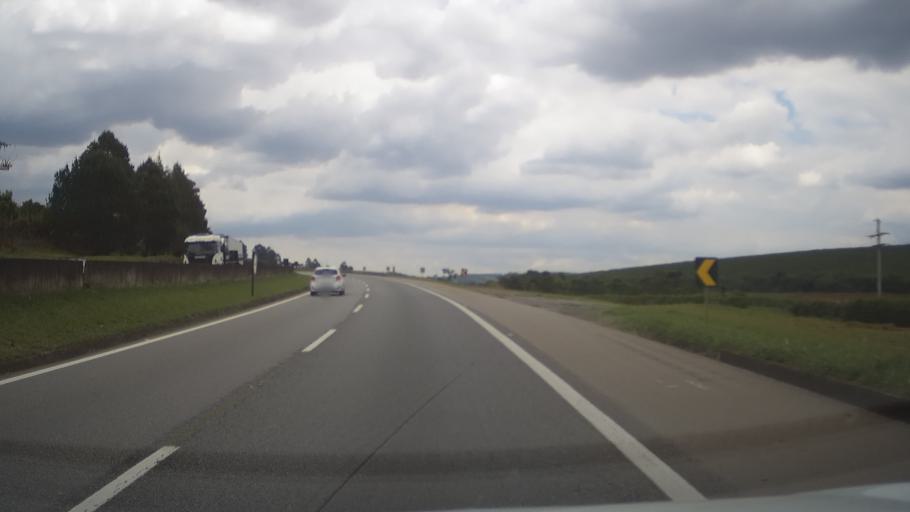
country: BR
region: Minas Gerais
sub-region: Tres Coracoes
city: Tres Coracoes
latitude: -21.5107
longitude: -45.2160
